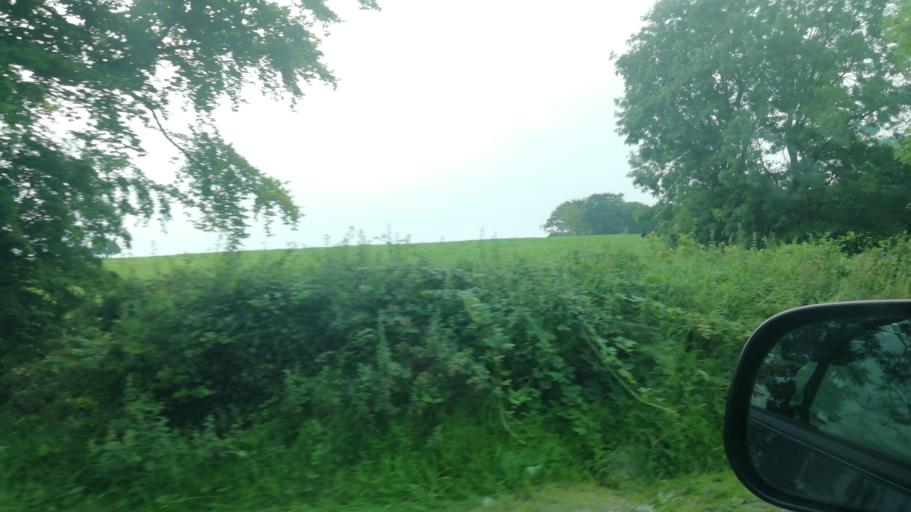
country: IE
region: Munster
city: Fethard
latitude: 52.5771
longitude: -7.6436
